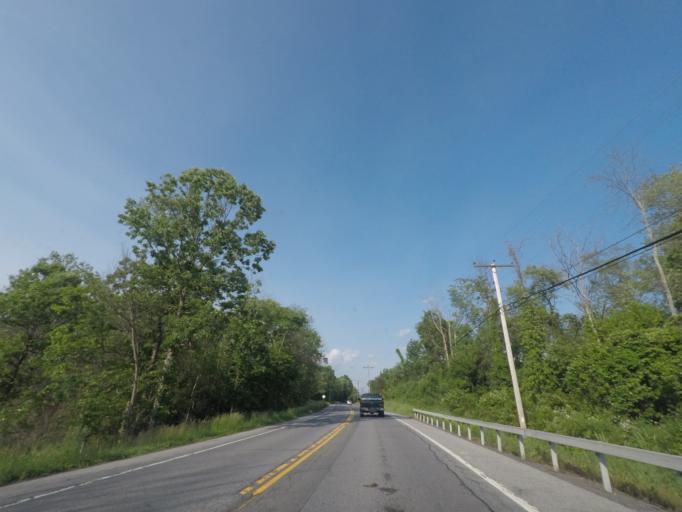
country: US
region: New York
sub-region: Orange County
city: Beaverdam Lake-Salisbury Mills
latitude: 41.4793
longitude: -74.1210
